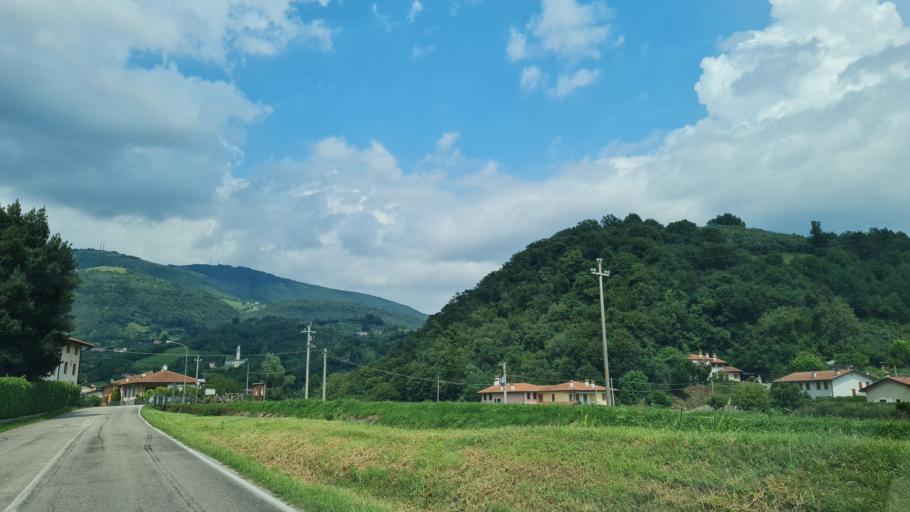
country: IT
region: Veneto
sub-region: Provincia di Vicenza
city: Marostica
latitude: 45.7608
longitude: 11.6608
